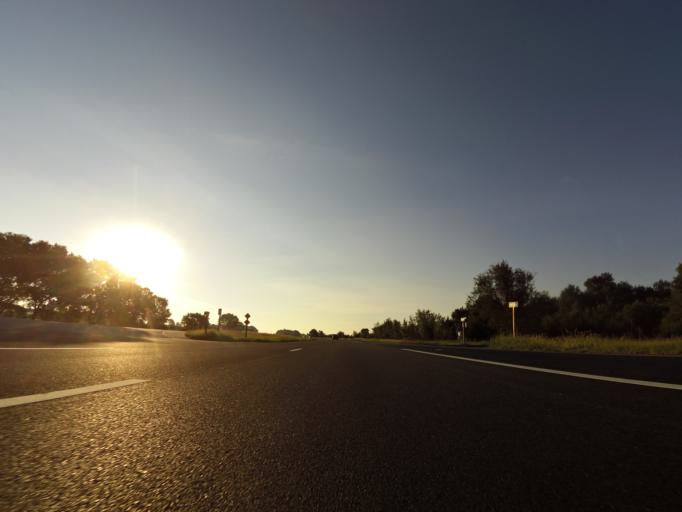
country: US
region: Kansas
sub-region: Sedgwick County
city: Colwich
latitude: 37.8270
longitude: -97.5558
